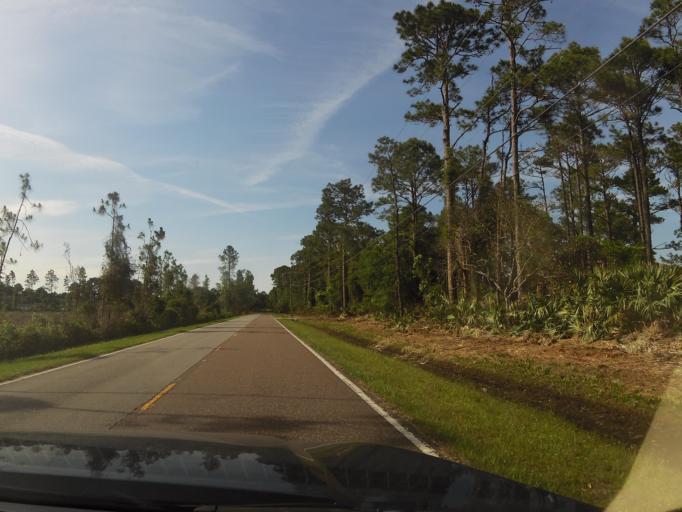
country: US
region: Florida
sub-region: Nassau County
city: Fernandina Beach
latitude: 30.5079
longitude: -81.4747
